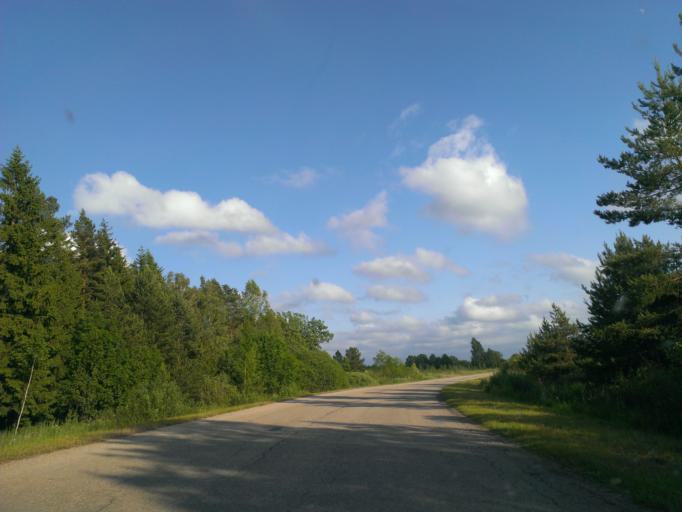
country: LV
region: Aizpute
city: Aizpute
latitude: 56.7891
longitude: 21.5125
